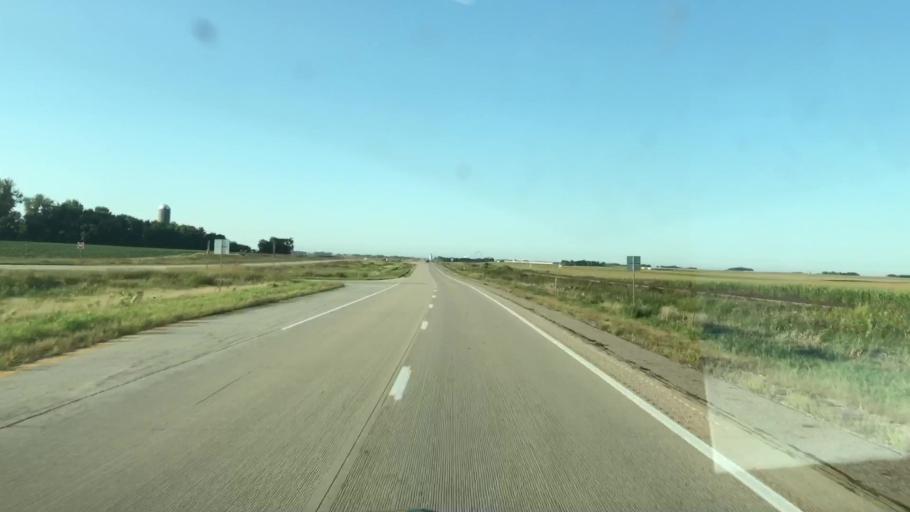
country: US
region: Iowa
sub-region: Osceola County
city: Sibley
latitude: 43.3716
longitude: -95.7629
